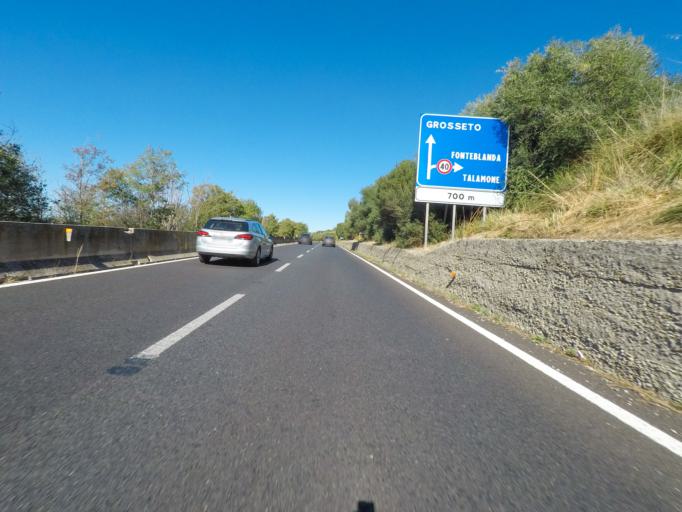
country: IT
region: Tuscany
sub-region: Provincia di Grosseto
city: Fonteblanda
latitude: 42.5598
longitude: 11.1722
